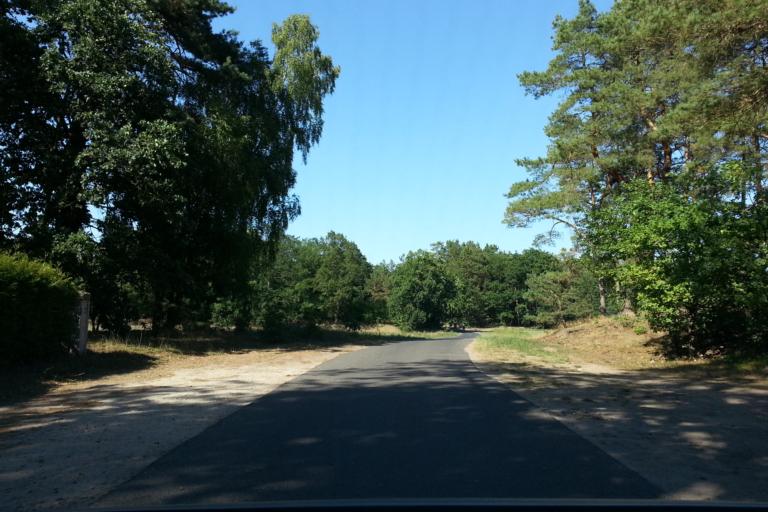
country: DE
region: Mecklenburg-Vorpommern
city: Torgelow
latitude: 53.6660
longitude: 14.0355
